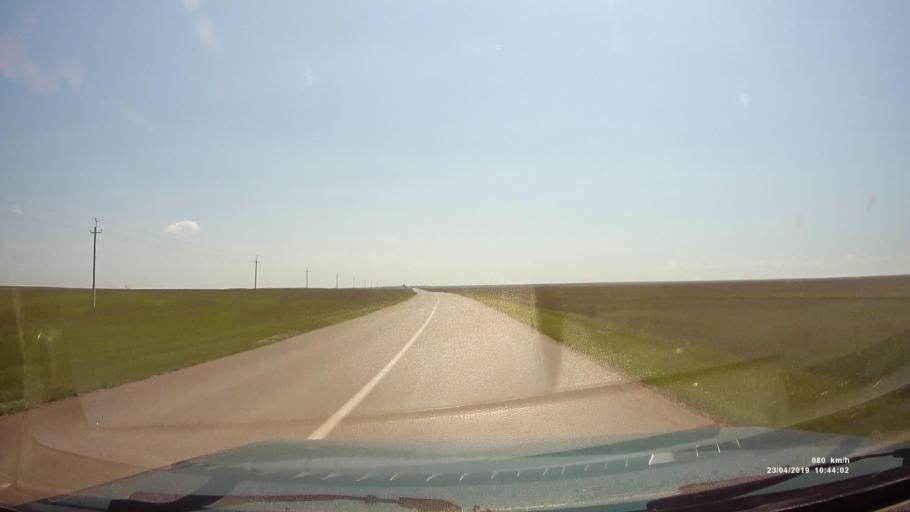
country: RU
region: Kalmykiya
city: Yashalta
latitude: 46.4631
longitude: 42.6514
